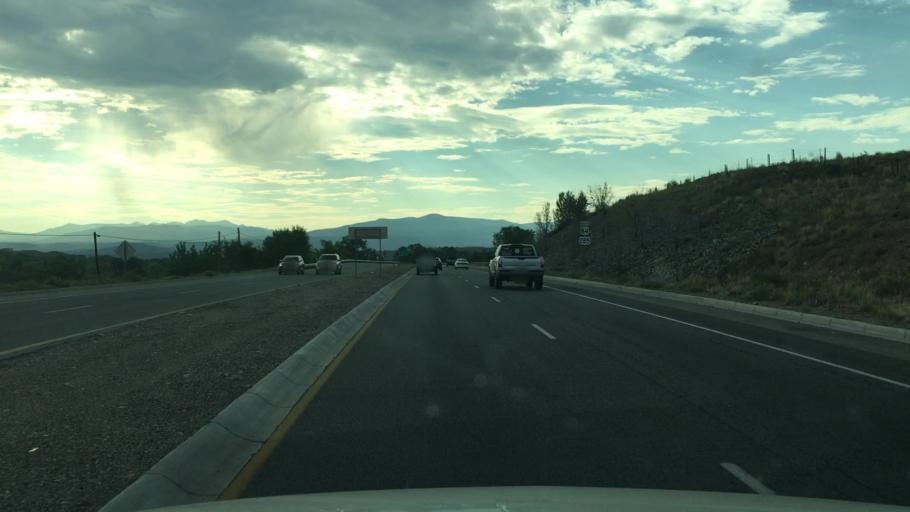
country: US
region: New Mexico
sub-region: Rio Arriba County
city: Espanola
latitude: 35.9865
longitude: -106.0564
